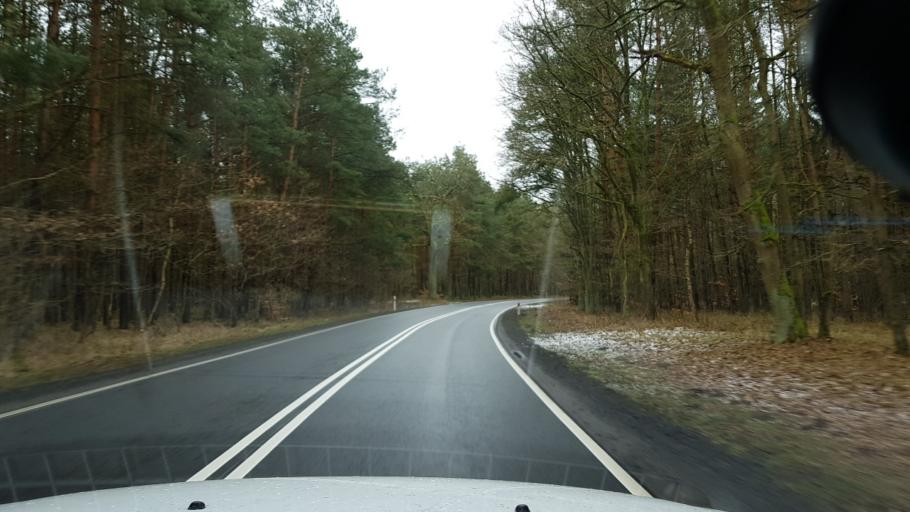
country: PL
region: West Pomeranian Voivodeship
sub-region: Powiat goleniowski
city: Stepnica
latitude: 53.6416
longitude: 14.6604
